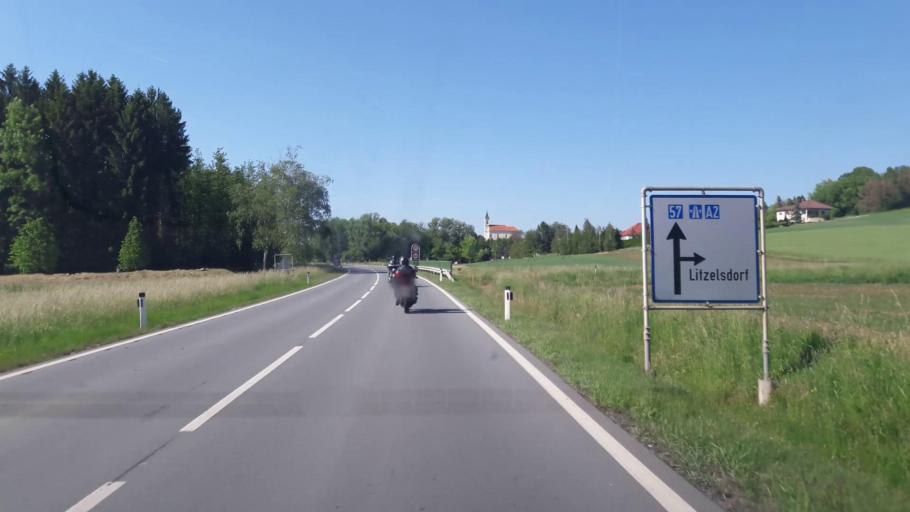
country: AT
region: Burgenland
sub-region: Politischer Bezirk Oberwart
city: Litzelsdorf
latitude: 47.2008
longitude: 16.1607
